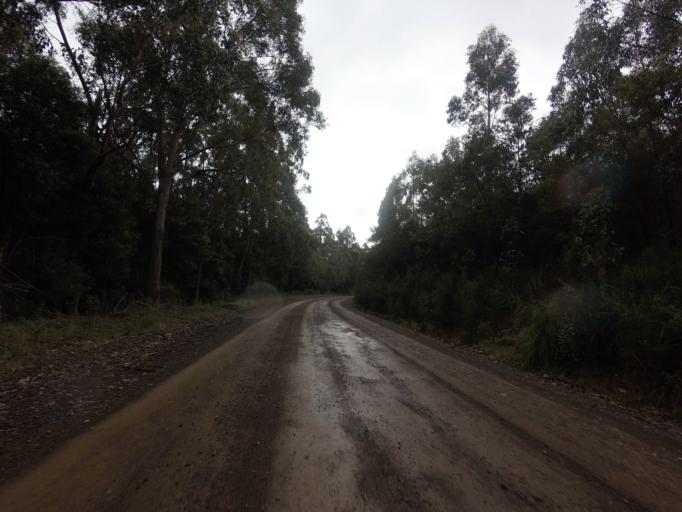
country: AU
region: Tasmania
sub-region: Huon Valley
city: Geeveston
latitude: -43.4696
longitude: 146.8926
